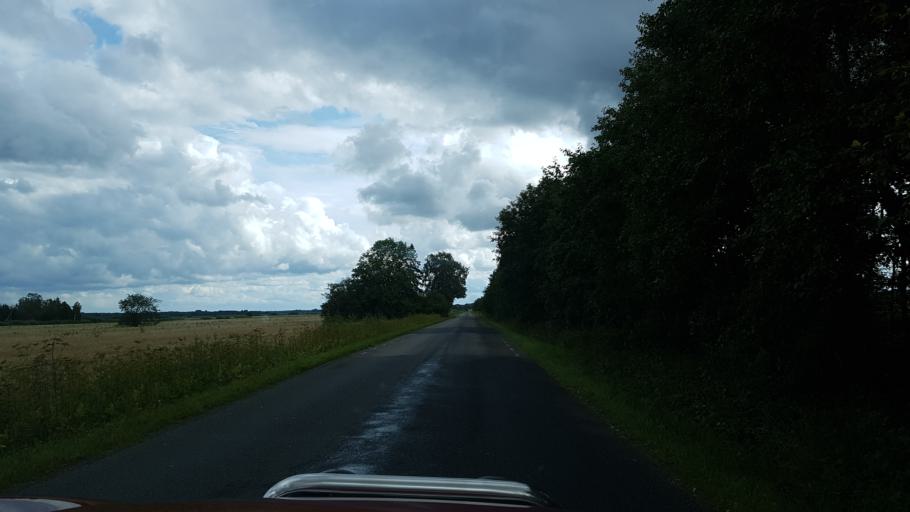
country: EE
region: Laeaene
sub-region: Lihula vald
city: Lihula
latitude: 58.7209
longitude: 23.9736
